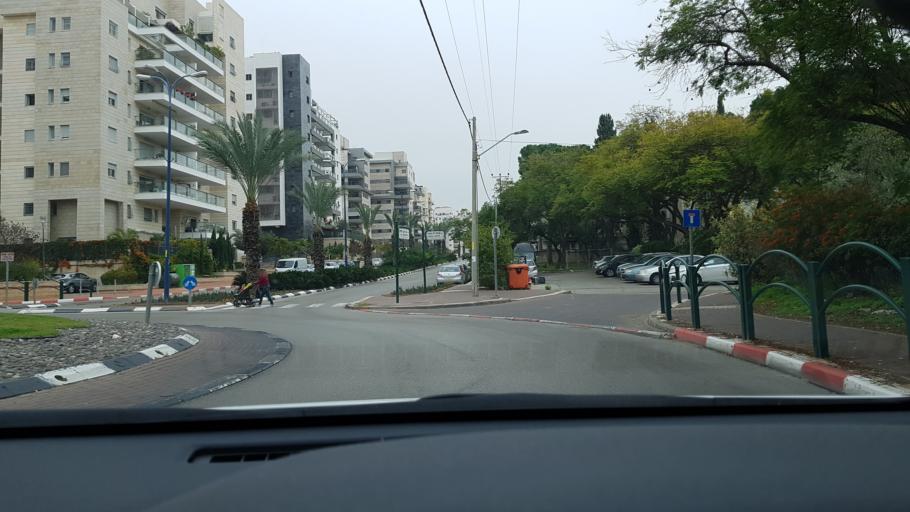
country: IL
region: Central District
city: Ness Ziona
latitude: 31.9050
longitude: 34.8182
